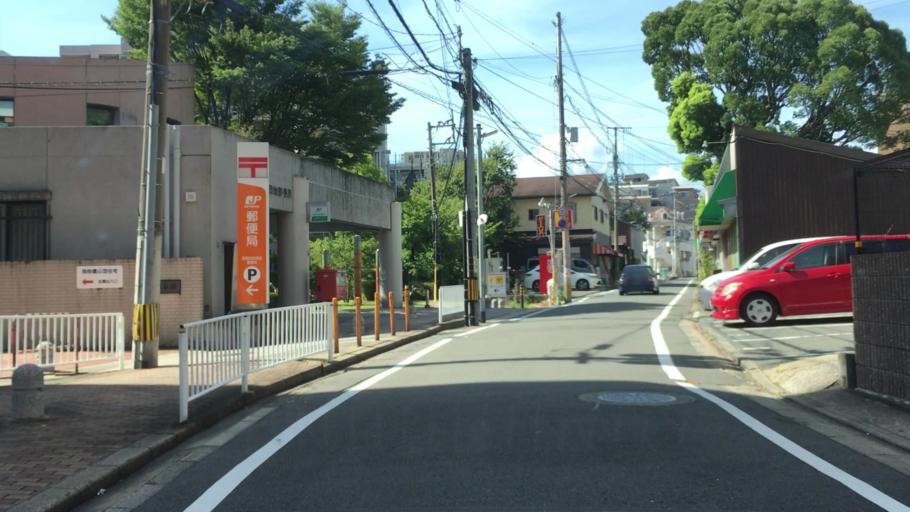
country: JP
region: Fukuoka
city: Fukuoka-shi
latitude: 33.5755
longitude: 130.3740
